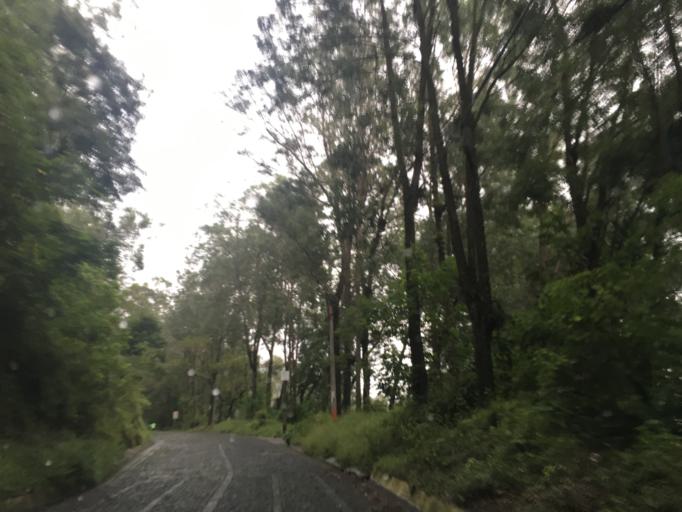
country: GT
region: Sacatepequez
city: Antigua Guatemala
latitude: 14.5652
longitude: -90.7294
